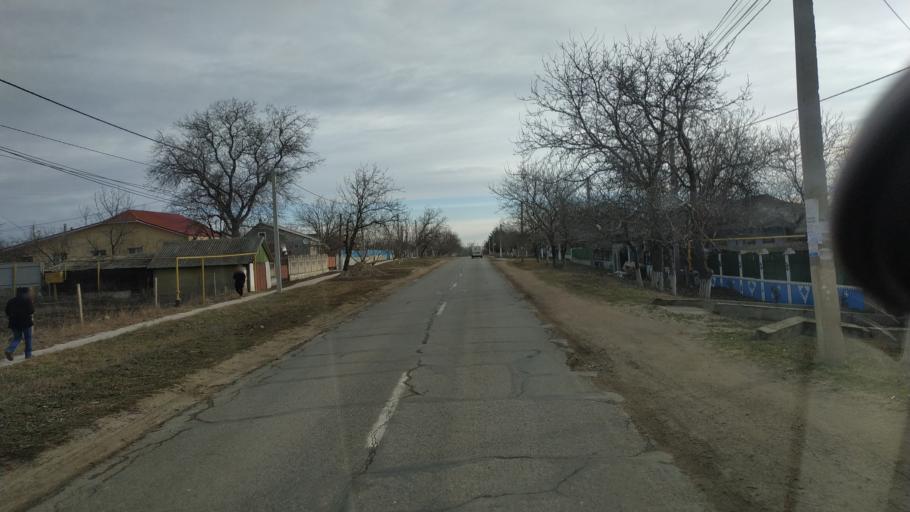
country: MD
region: Criuleni
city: Criuleni
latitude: 47.1598
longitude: 29.1144
